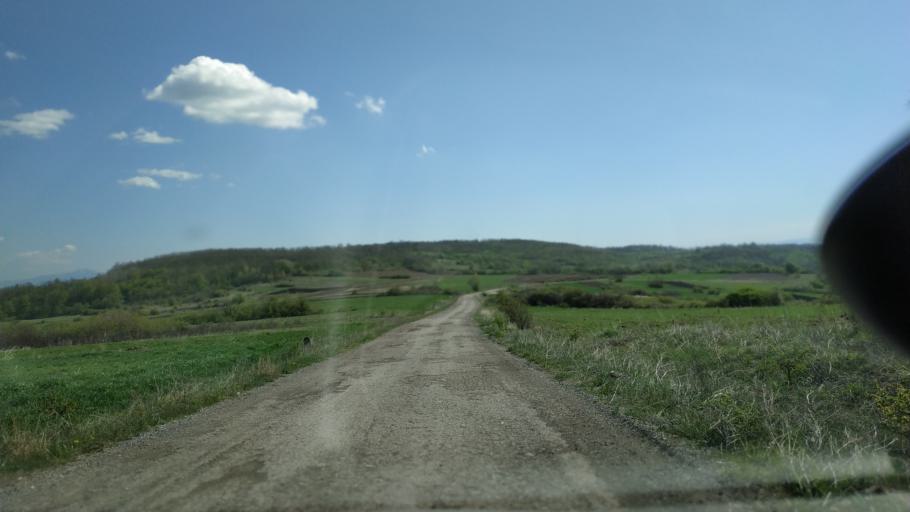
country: RS
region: Central Serbia
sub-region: Zajecarski Okrug
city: Soko Banja
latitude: 43.5176
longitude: 21.9056
